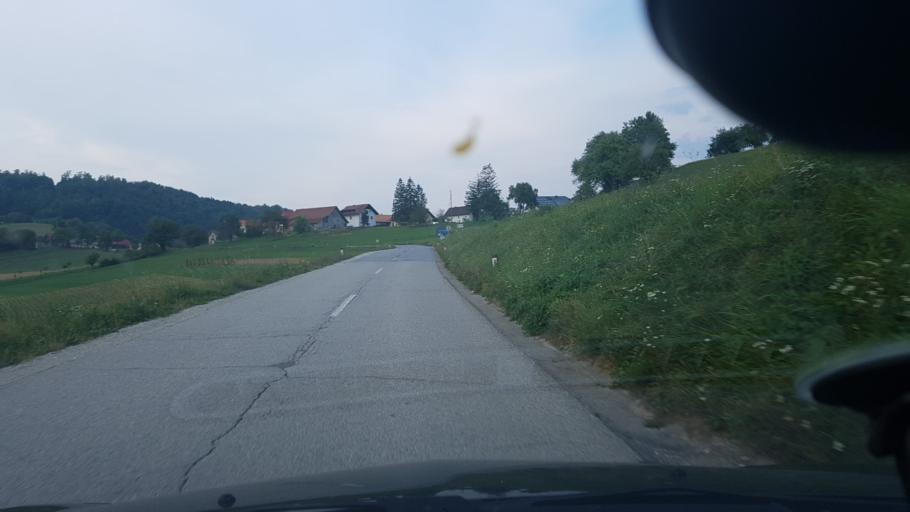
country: SI
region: Kozje
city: Kozje
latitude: 46.0345
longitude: 15.5721
